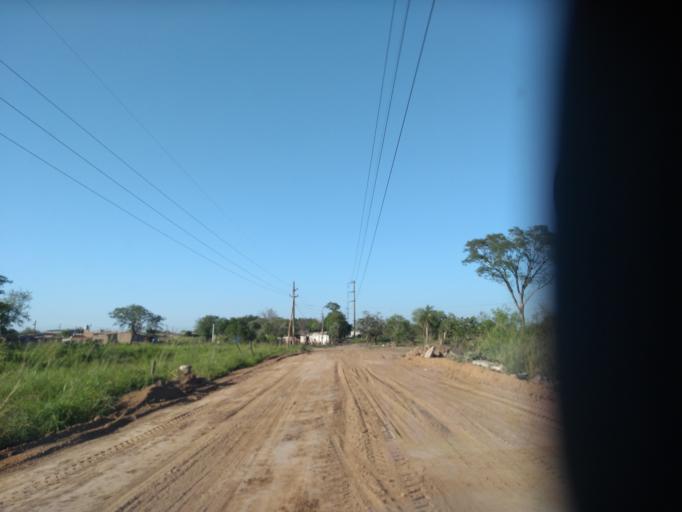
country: AR
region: Chaco
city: Fontana
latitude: -27.4148
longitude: -59.0195
